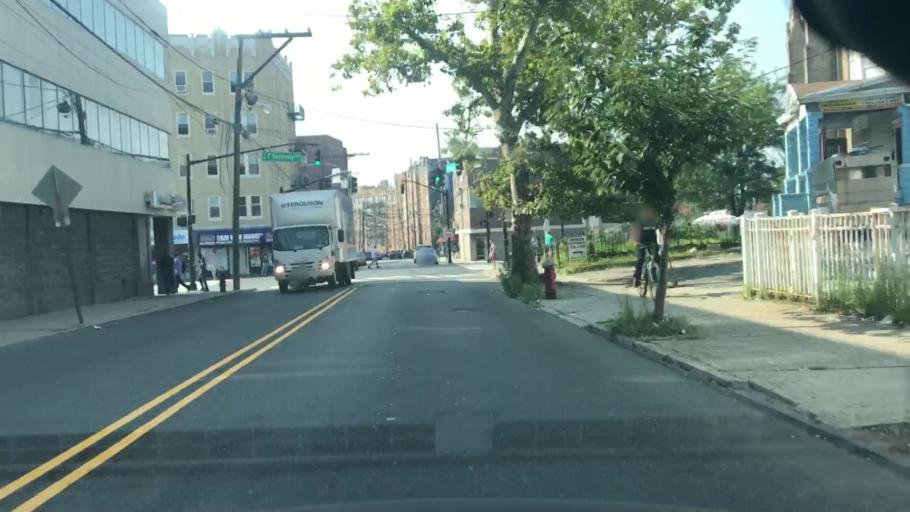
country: US
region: New Jersey
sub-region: Hudson County
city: Jersey City
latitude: 40.7323
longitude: -74.0672
